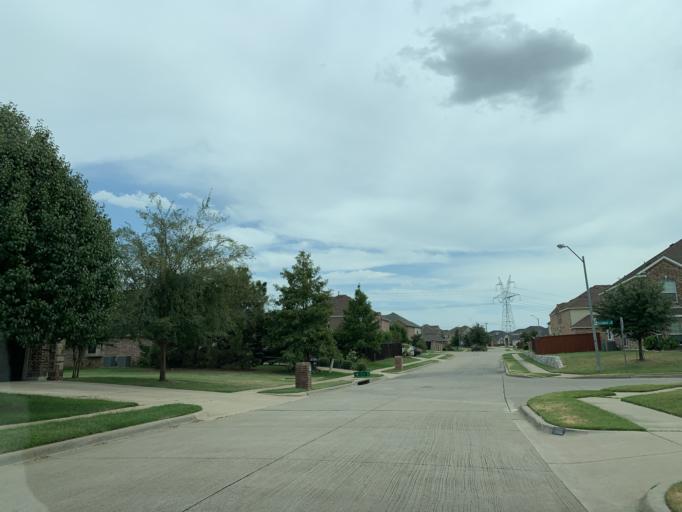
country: US
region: Texas
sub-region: Tarrant County
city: Arlington
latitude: 32.6556
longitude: -97.0456
